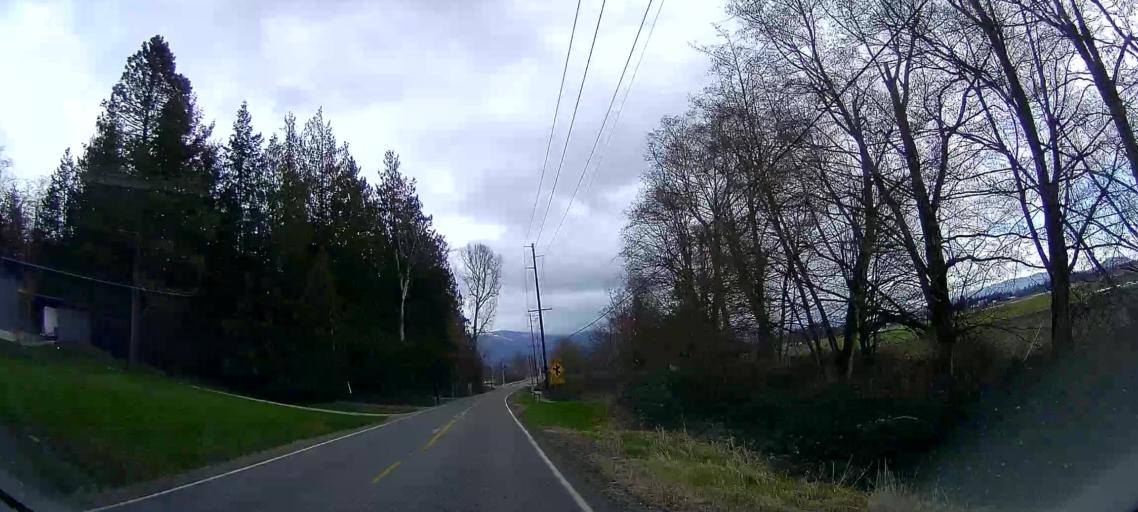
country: US
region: Washington
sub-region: Skagit County
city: Sedro-Woolley
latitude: 48.5309
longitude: -122.2825
